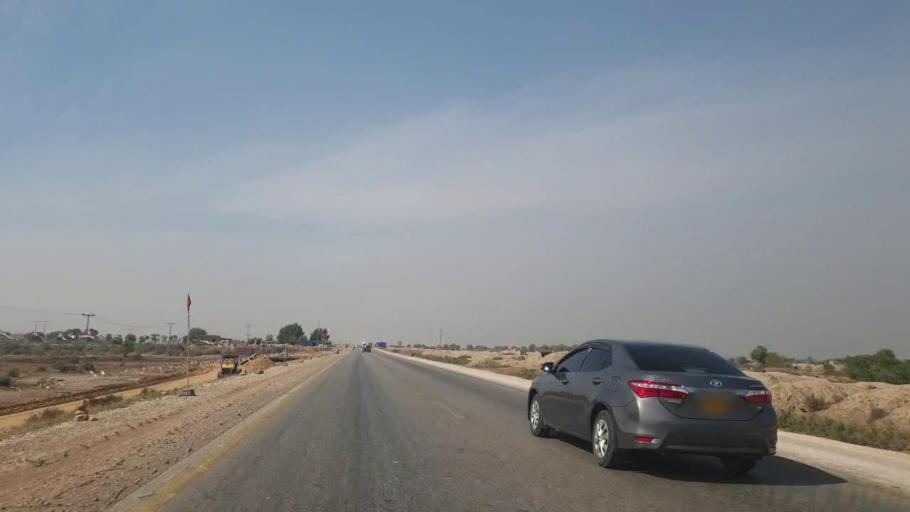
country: PK
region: Sindh
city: Sann
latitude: 25.9974
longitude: 68.1665
